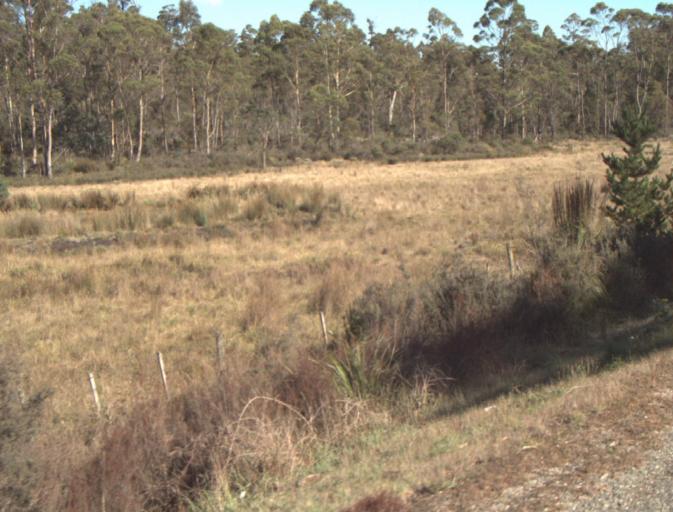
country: AU
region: Tasmania
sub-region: Launceston
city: Mayfield
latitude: -41.3262
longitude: 147.1847
